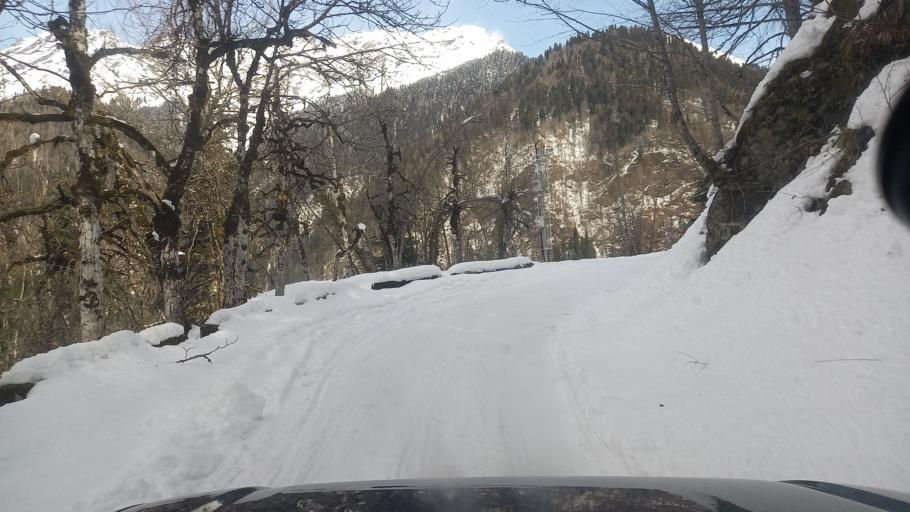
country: GE
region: Abkhazia
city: Gagra
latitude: 43.4795
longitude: 40.5485
